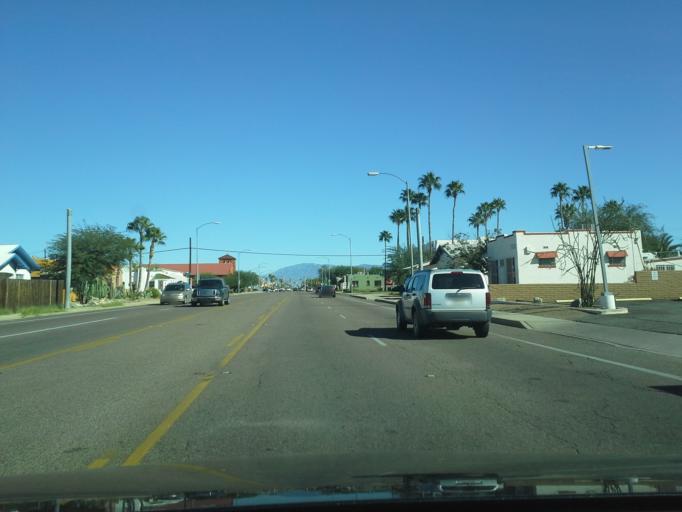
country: US
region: Arizona
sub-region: Pima County
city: Tucson
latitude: 32.2214
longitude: -110.9478
